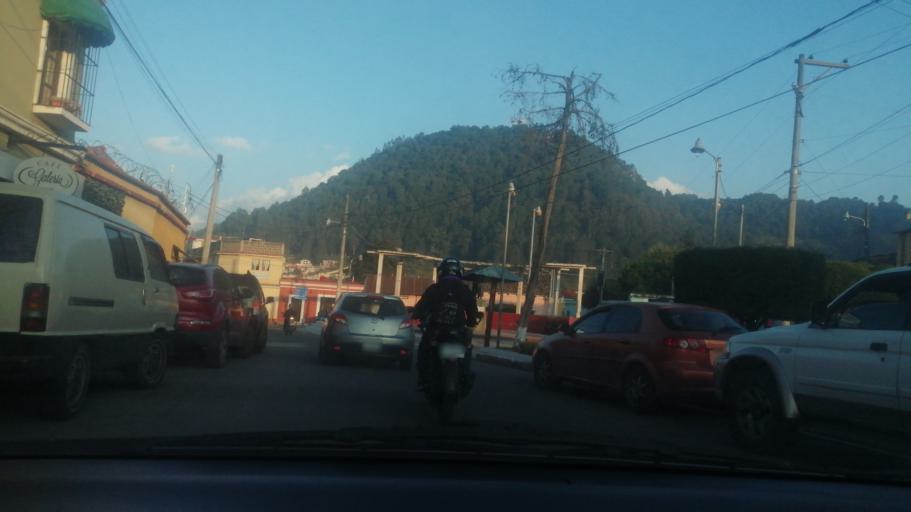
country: GT
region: Quetzaltenango
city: Quetzaltenango
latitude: 14.8323
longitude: -91.5133
